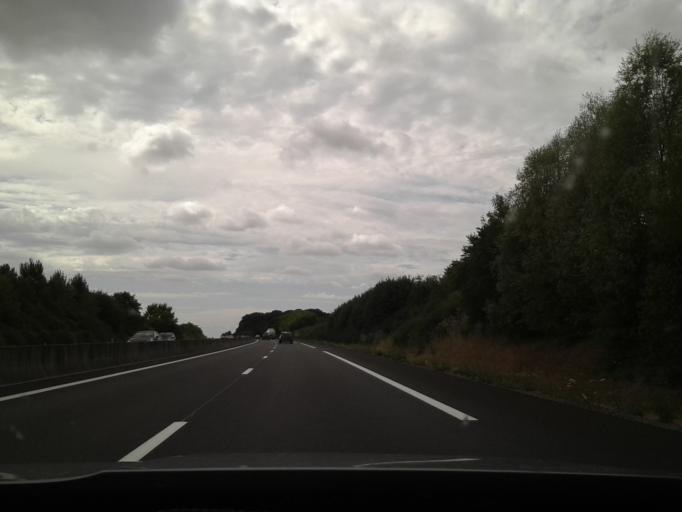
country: FR
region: Pays de la Loire
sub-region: Departement de la Sarthe
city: Arconnay
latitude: 48.3491
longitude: 0.0971
